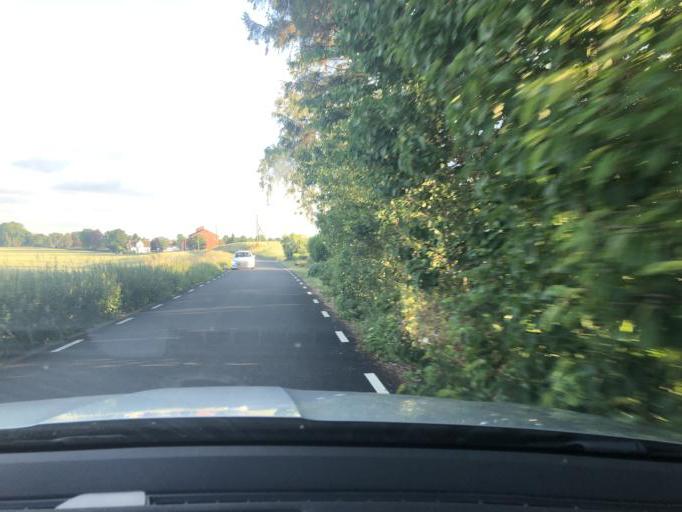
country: SE
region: Skane
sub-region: Simrishamns Kommun
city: Simrishamn
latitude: 55.4654
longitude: 14.1903
